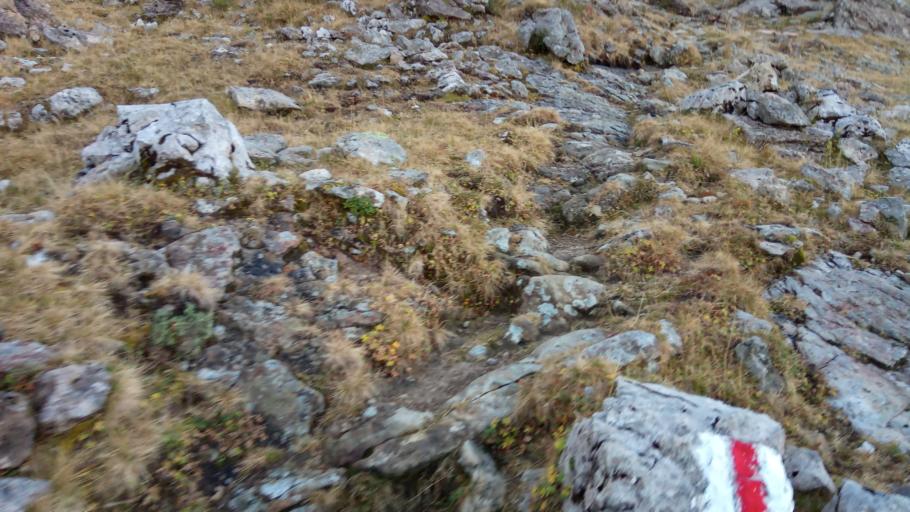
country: CH
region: Bern
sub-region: Interlaken-Oberhasli District
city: Beatenberg
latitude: 46.7460
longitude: 7.7906
